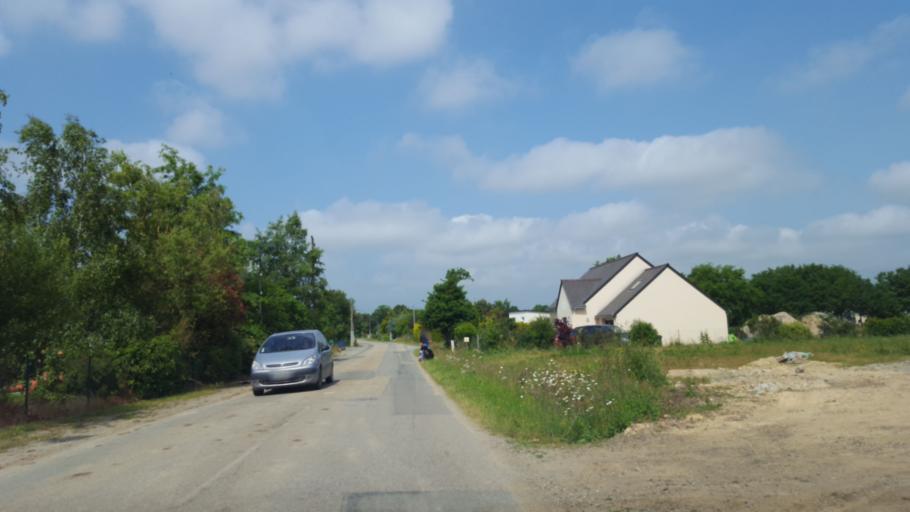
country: FR
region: Brittany
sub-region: Departement d'Ille-et-Vilaine
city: Guignen
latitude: 47.9213
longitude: -1.8707
